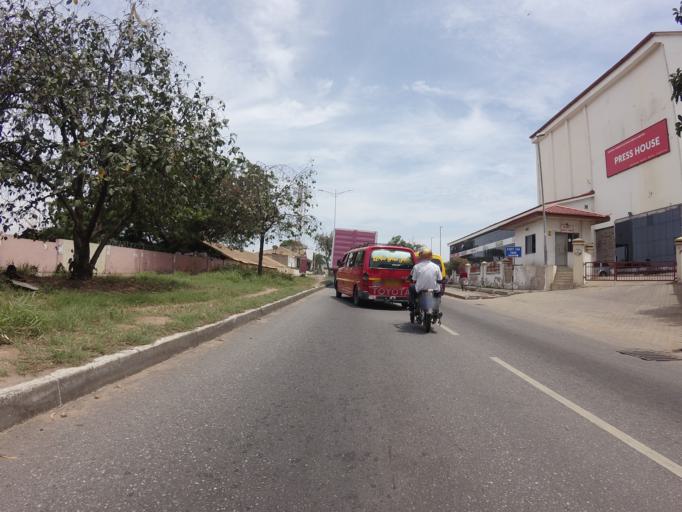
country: GH
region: Greater Accra
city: Accra
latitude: 5.5545
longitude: -0.2154
